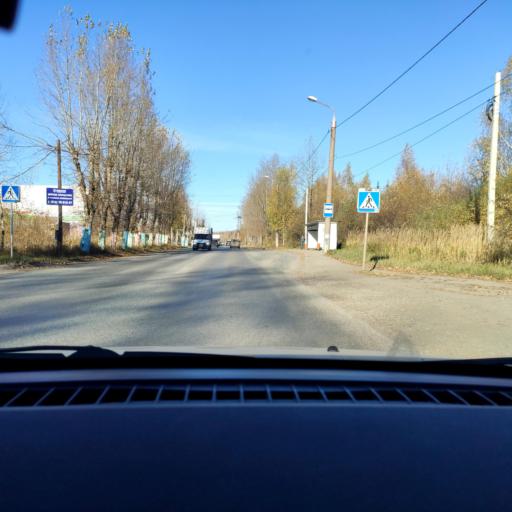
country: RU
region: Perm
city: Perm
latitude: 58.1049
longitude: 56.3610
